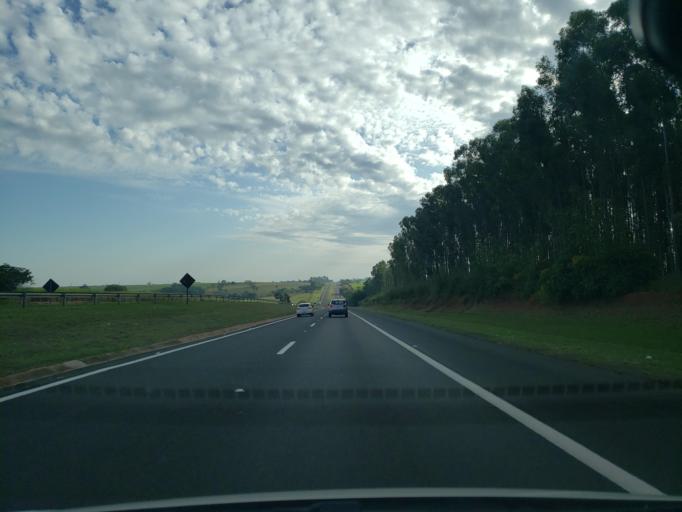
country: BR
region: Sao Paulo
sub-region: Guararapes
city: Guararapes
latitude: -21.1998
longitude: -50.5705
